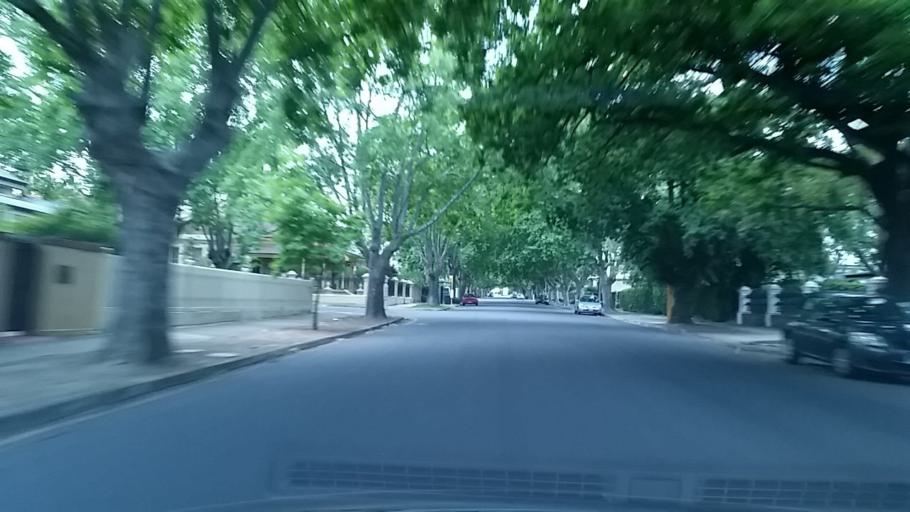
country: AU
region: South Australia
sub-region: Norwood Payneham St Peters
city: Royston Park
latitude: -34.9106
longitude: 138.6213
